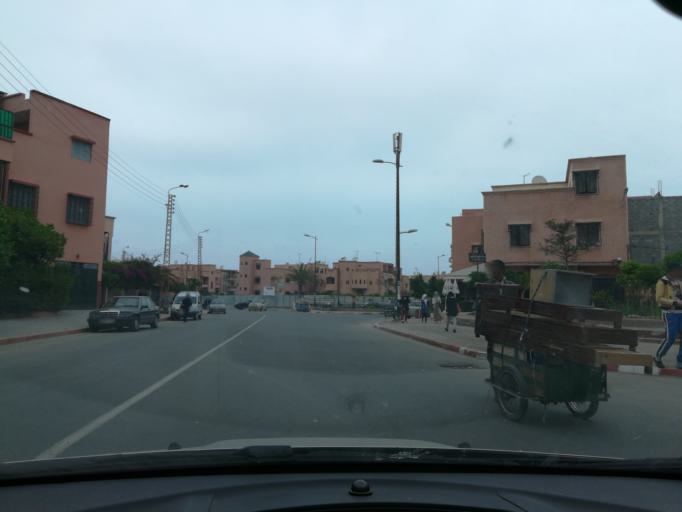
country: MA
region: Marrakech-Tensift-Al Haouz
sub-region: Marrakech
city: Marrakesh
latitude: 31.6595
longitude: -7.9971
